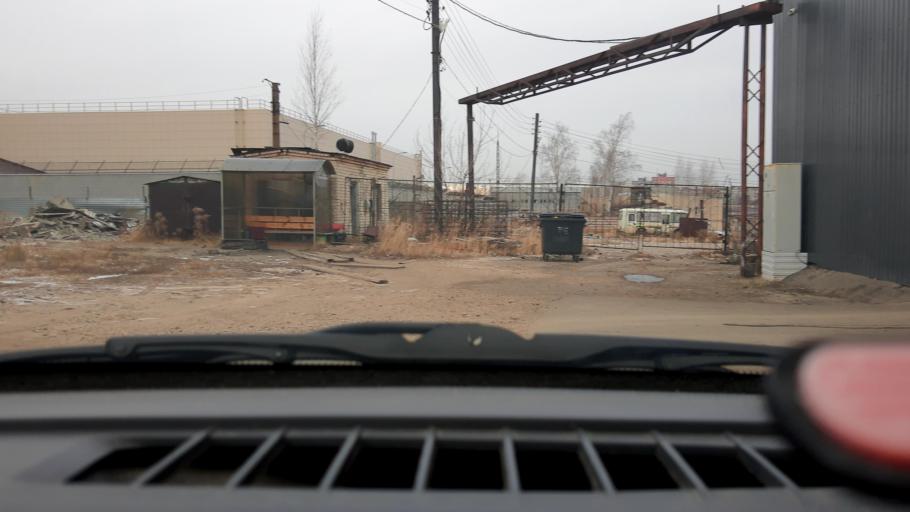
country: RU
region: Nizjnij Novgorod
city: Bor
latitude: 56.3078
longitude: 44.0589
